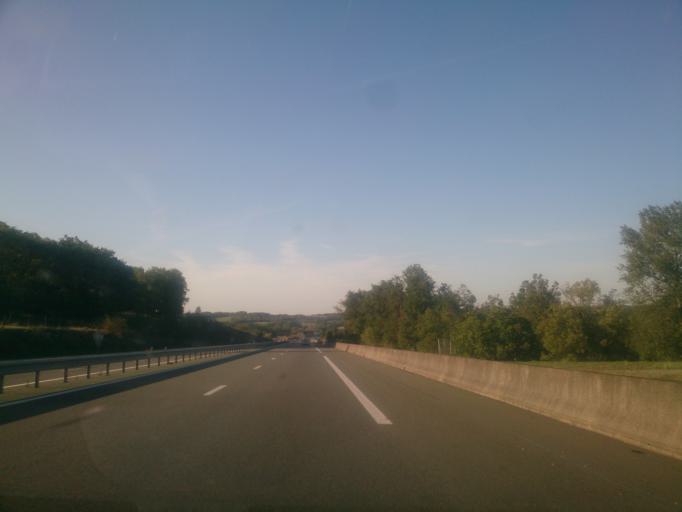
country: FR
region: Midi-Pyrenees
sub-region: Departement du Lot
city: Le Vigan
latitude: 44.6805
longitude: 1.5716
